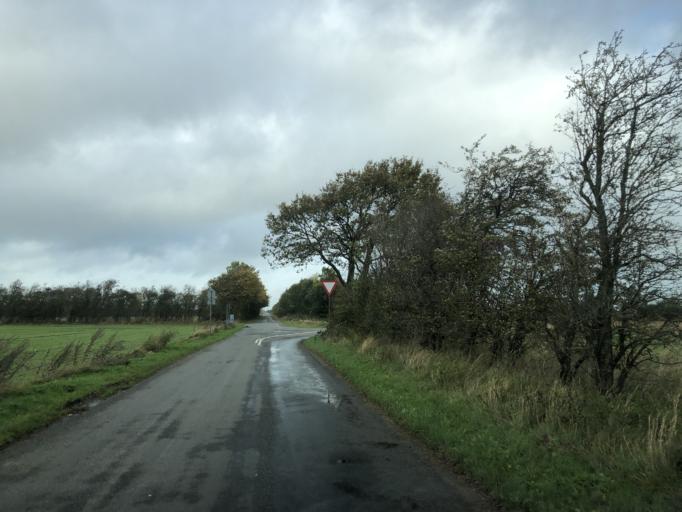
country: DK
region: South Denmark
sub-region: Vejen Kommune
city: Vejen
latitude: 55.4521
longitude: 9.1097
